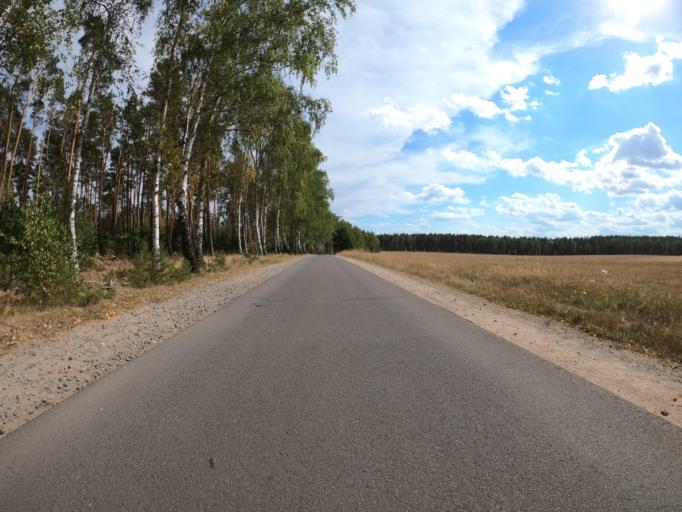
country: DE
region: Brandenburg
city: Lychen
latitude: 53.2934
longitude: 13.4287
